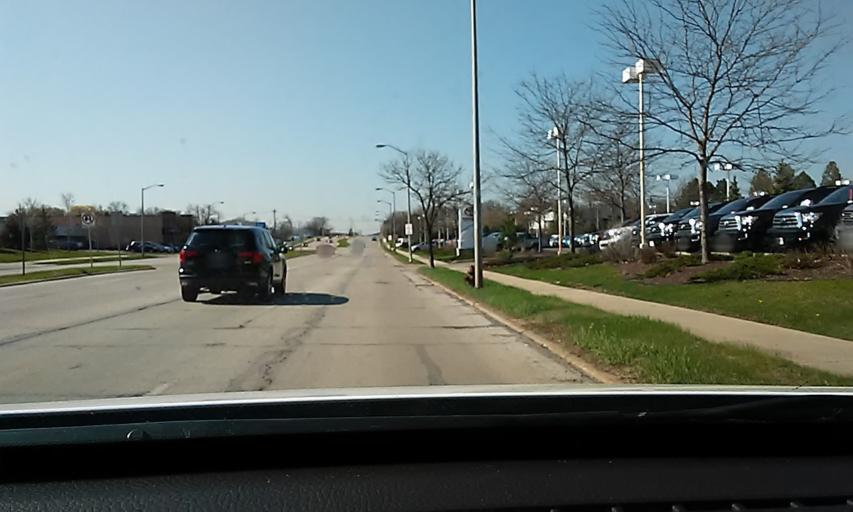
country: US
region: Wisconsin
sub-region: Milwaukee County
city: Greenfield
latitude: 42.9842
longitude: -88.0474
